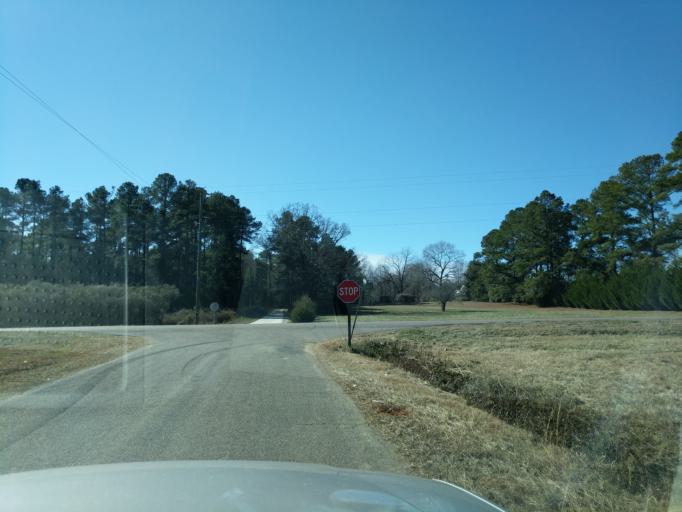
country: US
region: South Carolina
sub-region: Saluda County
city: Saluda
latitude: 34.0299
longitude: -81.8365
